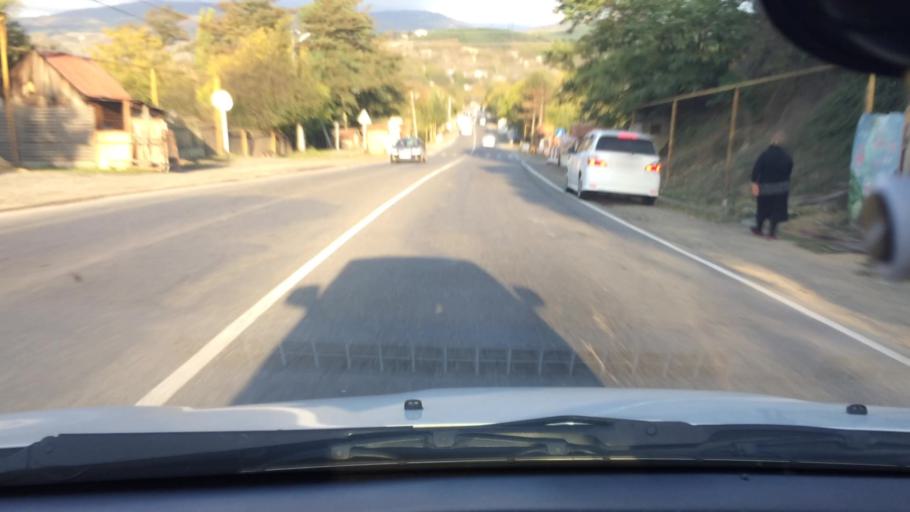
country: GE
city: Surami
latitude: 42.0279
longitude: 43.5544
